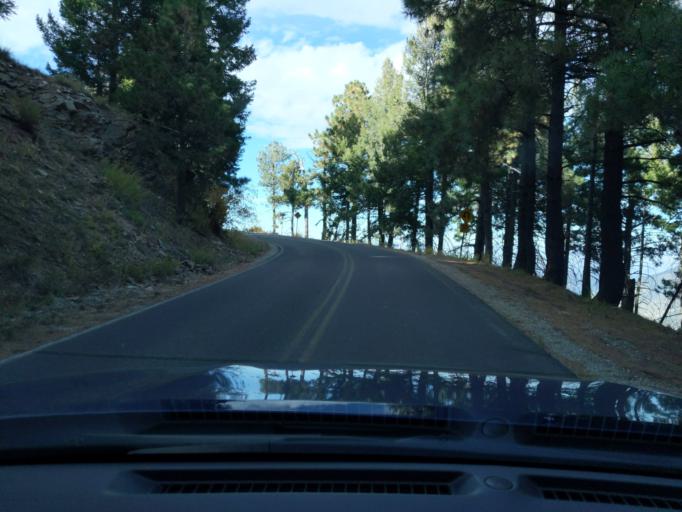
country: US
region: Arizona
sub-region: Pima County
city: Catalina
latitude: 32.4516
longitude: -110.7828
